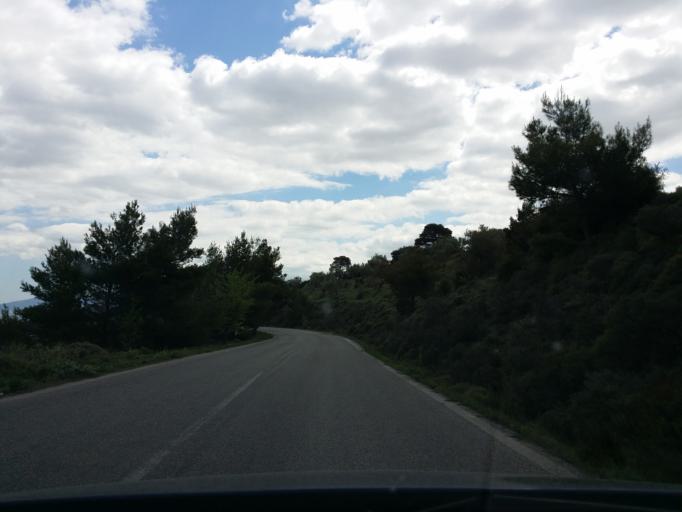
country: GR
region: Attica
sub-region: Nomarchia Dytikis Attikis
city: Fyli
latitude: 38.1201
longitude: 23.6512
